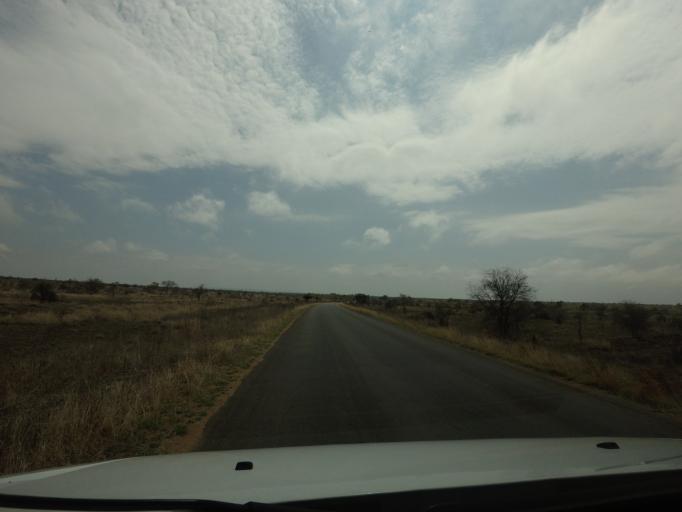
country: ZA
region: Limpopo
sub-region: Mopani District Municipality
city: Phalaborwa
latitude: -24.1708
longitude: 31.7173
